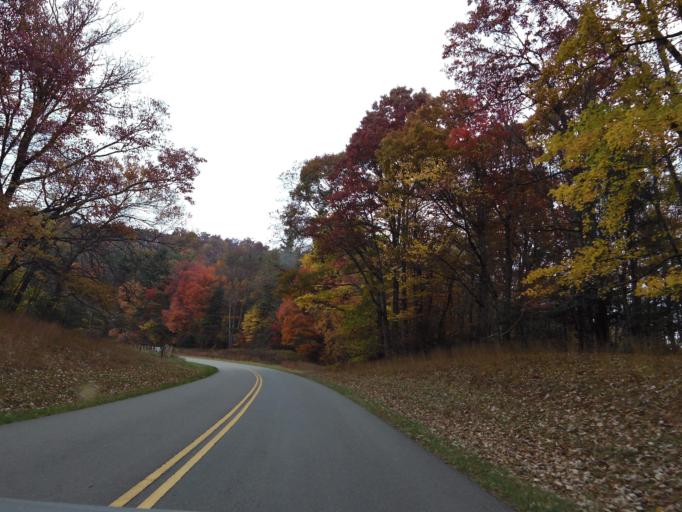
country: US
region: North Carolina
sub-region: Ashe County
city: Jefferson
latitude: 36.3750
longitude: -81.3197
